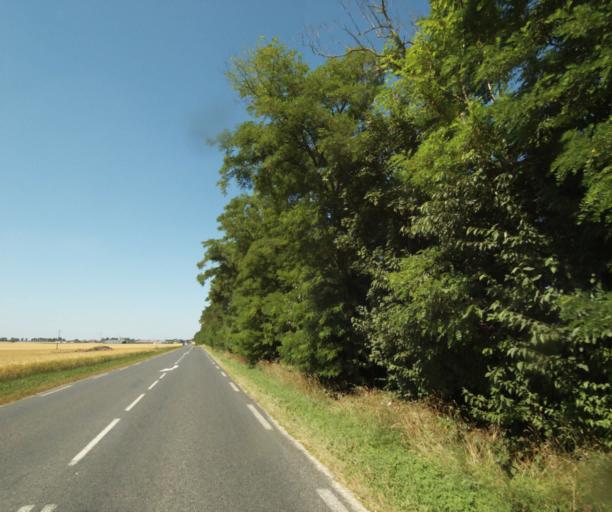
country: FR
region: Ile-de-France
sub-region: Departement de Seine-et-Marne
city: La Chapelle-la-Reine
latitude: 48.2986
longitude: 2.5739
